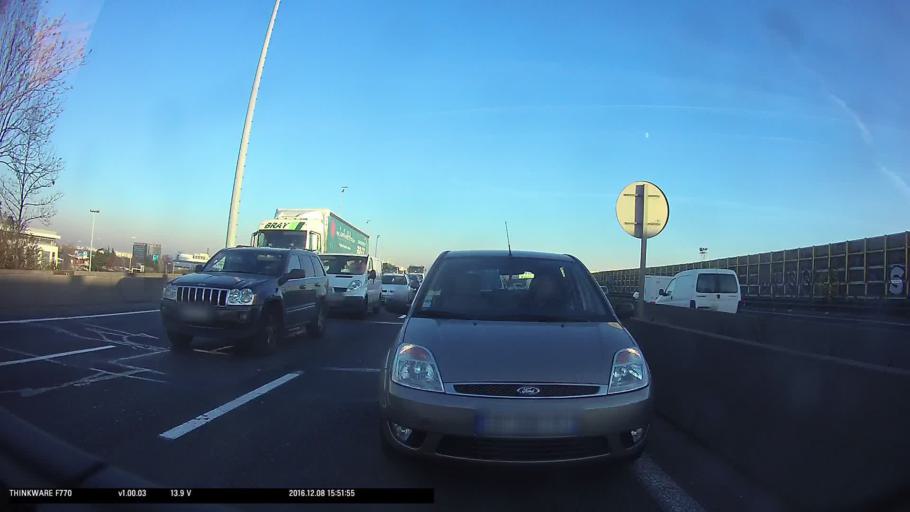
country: FR
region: Ile-de-France
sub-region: Departement de Seine-Saint-Denis
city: Saint-Denis
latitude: 48.9228
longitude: 2.3458
